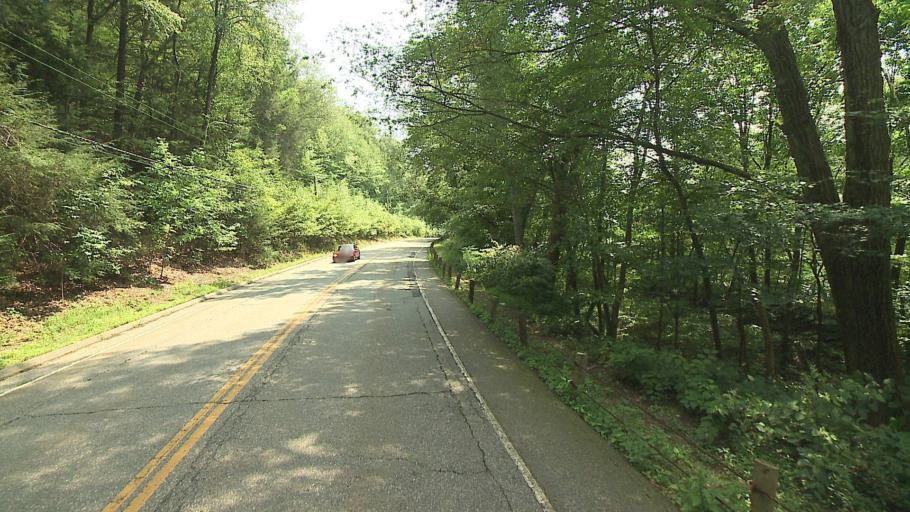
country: US
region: Connecticut
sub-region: Litchfield County
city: Oakville
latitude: 41.6179
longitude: -73.0576
